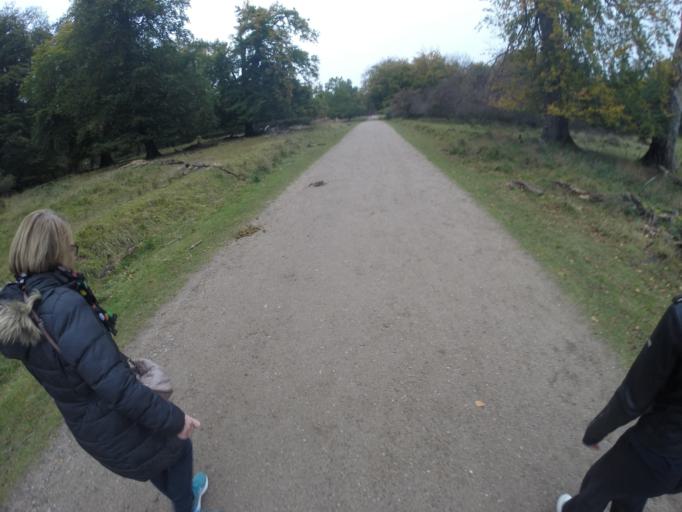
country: DK
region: Capital Region
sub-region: Lyngby-Tarbaek Kommune
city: Kongens Lyngby
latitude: 55.7756
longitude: 12.5492
